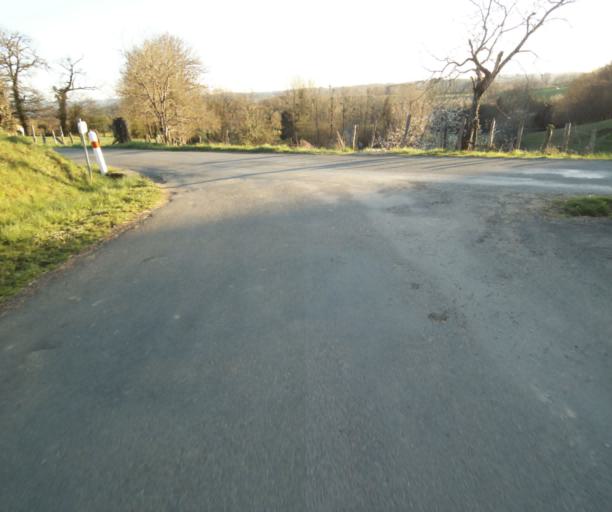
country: FR
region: Limousin
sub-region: Departement de la Correze
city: Saint-Clement
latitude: 45.3356
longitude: 1.7133
